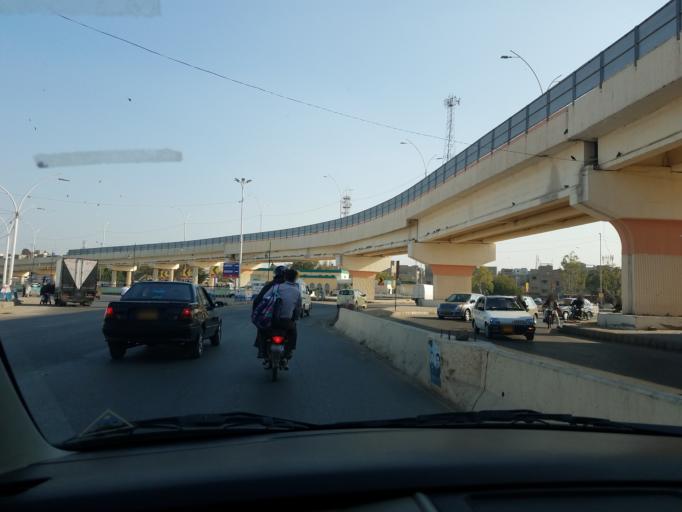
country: PK
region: Sindh
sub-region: Karachi District
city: Karachi
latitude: 24.8877
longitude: 67.1251
